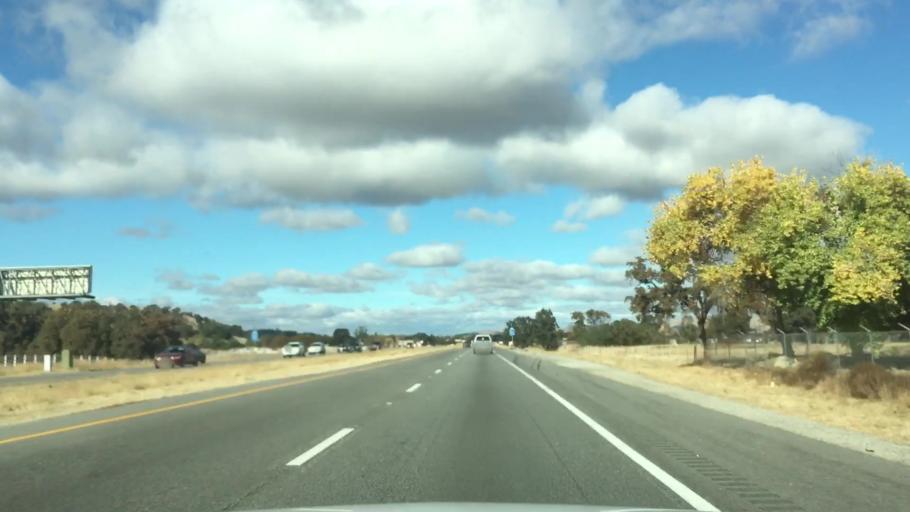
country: US
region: California
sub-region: San Luis Obispo County
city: Paso Robles
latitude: 35.6696
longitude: -120.6964
